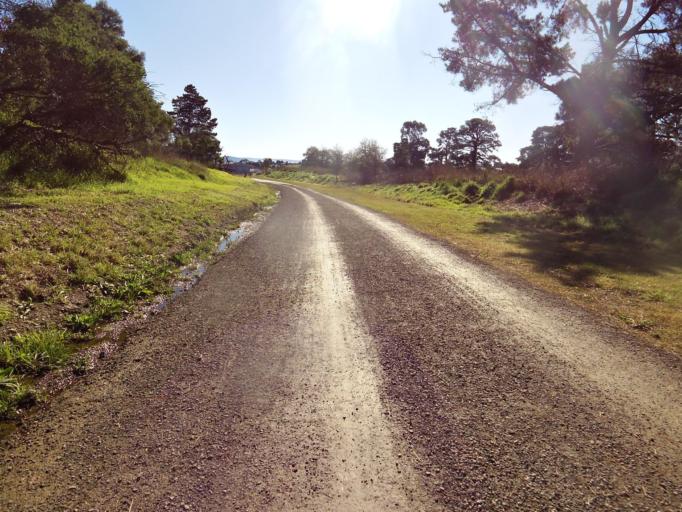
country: AU
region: Victoria
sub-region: Yarra Ranges
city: Lilydale
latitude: -37.7293
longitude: 145.3723
